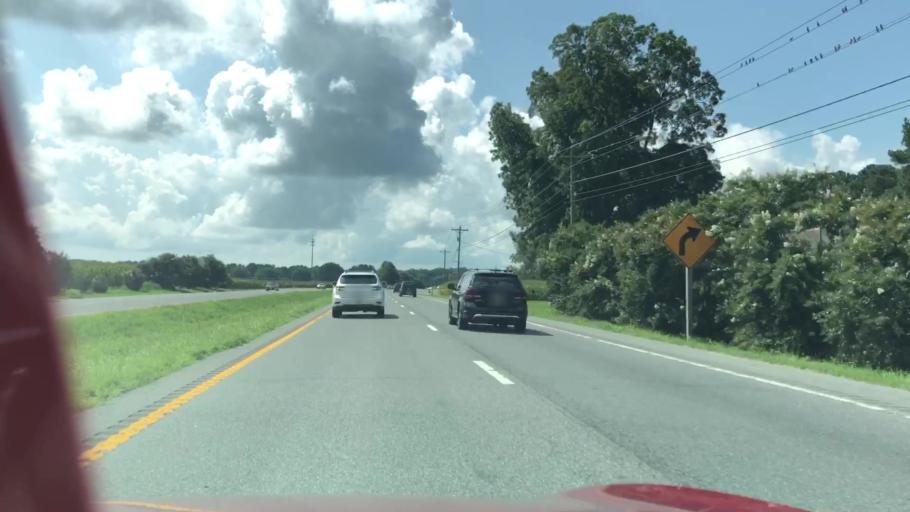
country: US
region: Virginia
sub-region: Accomack County
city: Wattsville
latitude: 37.8639
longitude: -75.5575
